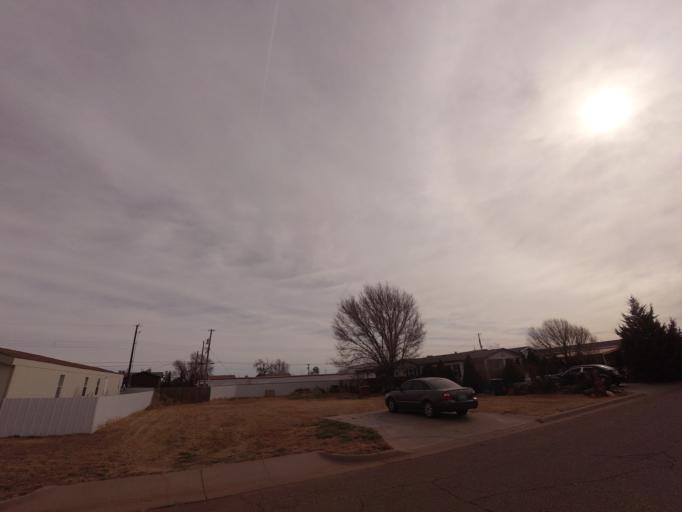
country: US
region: New Mexico
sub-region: Curry County
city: Clovis
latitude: 34.4056
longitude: -103.2467
